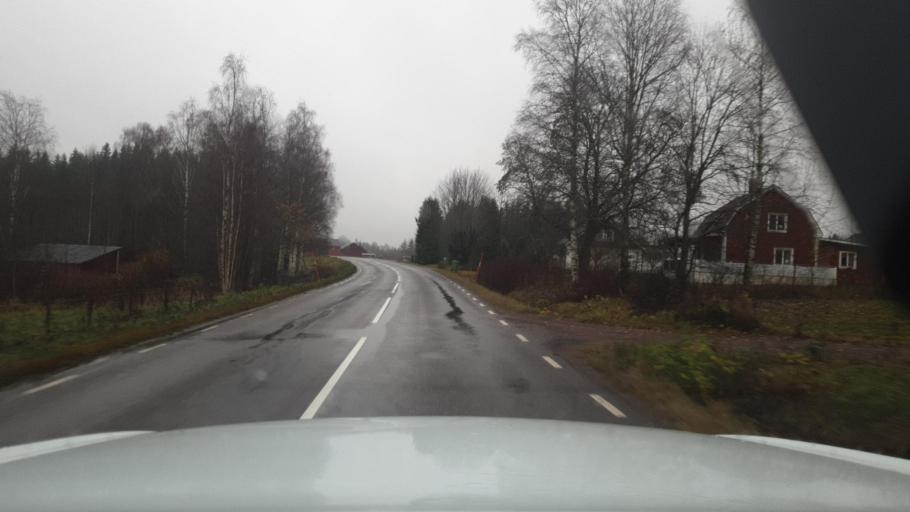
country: SE
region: Vaermland
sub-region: Sunne Kommun
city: Sunne
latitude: 59.7939
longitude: 13.0714
